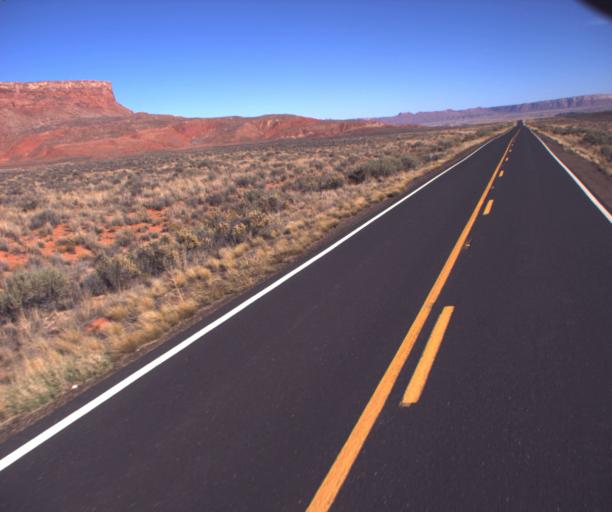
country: US
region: Arizona
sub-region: Coconino County
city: Page
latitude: 36.6934
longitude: -111.8977
